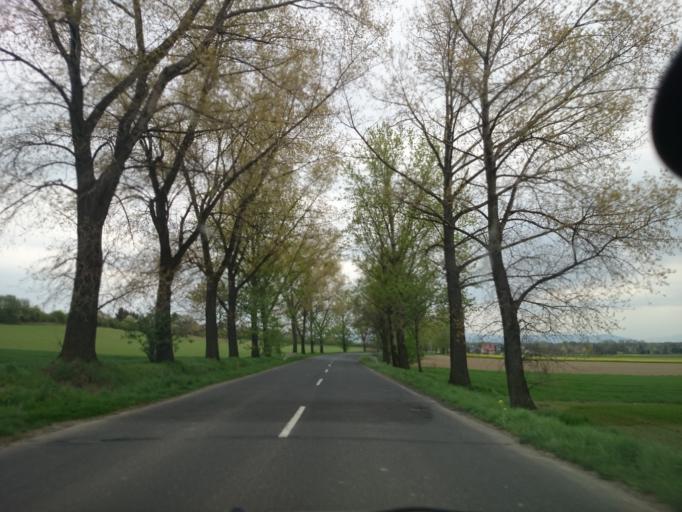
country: PL
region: Opole Voivodeship
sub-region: Powiat nyski
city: Nysa
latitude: 50.4202
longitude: 17.3382
